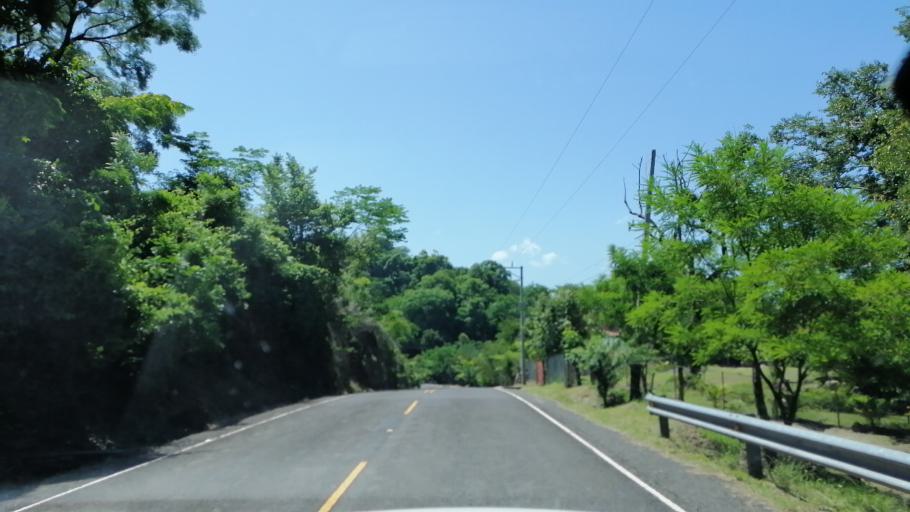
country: SV
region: San Miguel
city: Sesori
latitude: 13.8052
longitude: -88.3844
